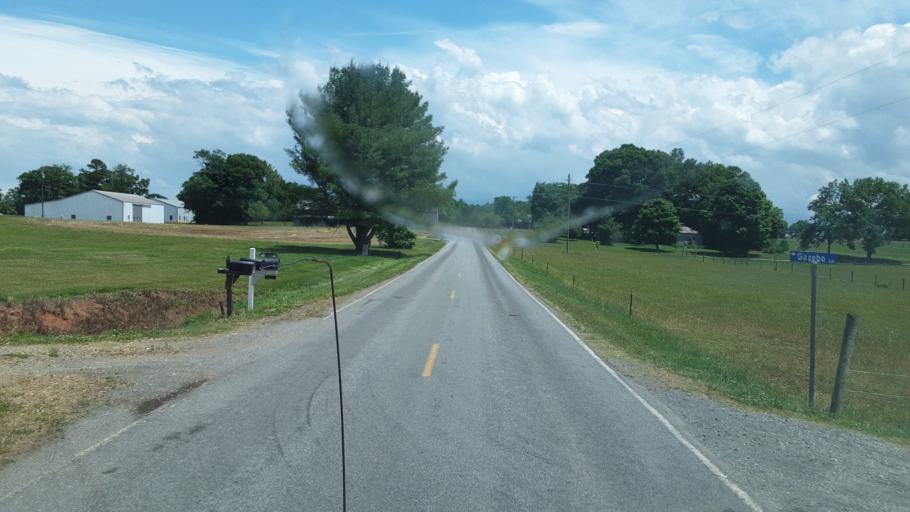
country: US
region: North Carolina
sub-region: Yadkin County
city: Jonesville
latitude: 36.0713
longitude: -80.8366
